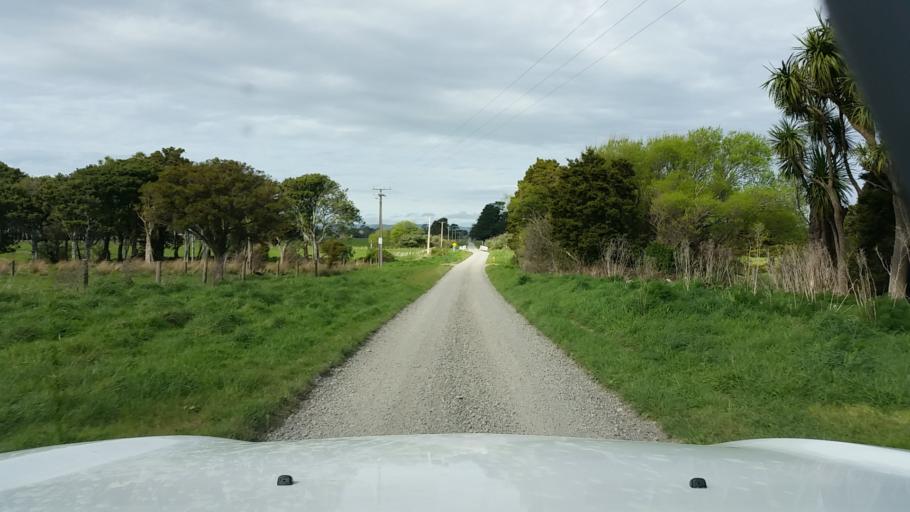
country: NZ
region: Wellington
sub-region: Upper Hutt City
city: Upper Hutt
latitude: -41.1325
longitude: 175.3254
